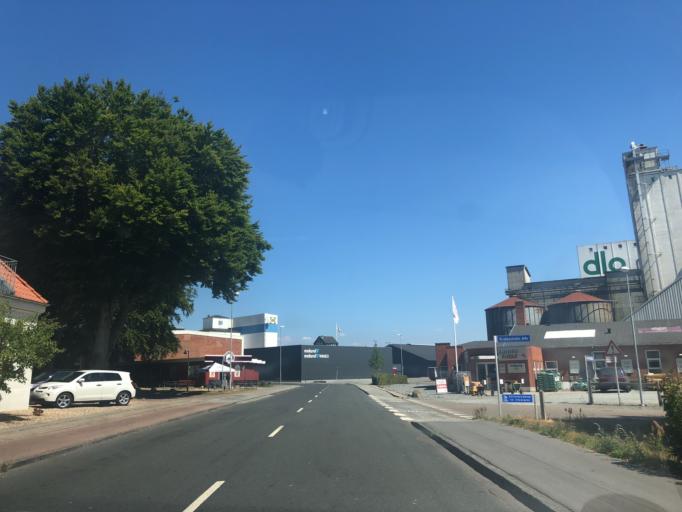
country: DK
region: Central Jutland
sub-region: Skive Kommune
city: Skive
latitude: 56.5703
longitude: 9.0503
